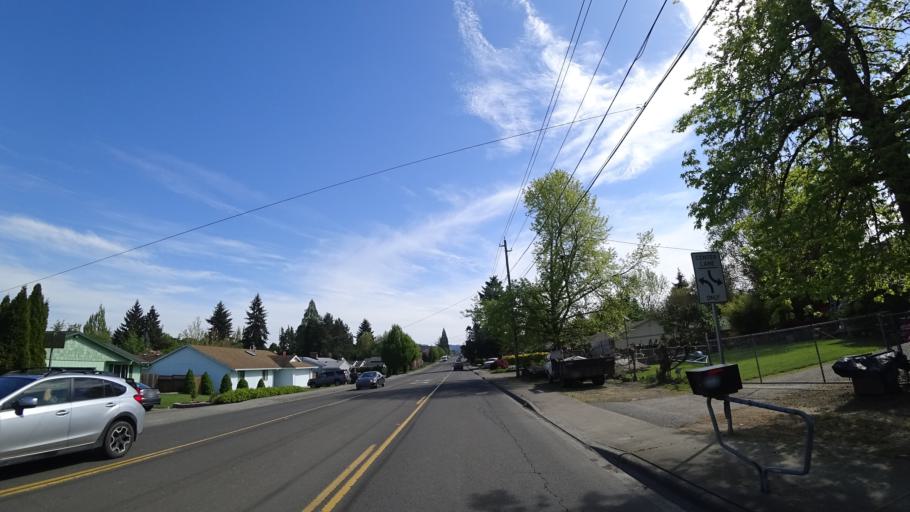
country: US
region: Oregon
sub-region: Washington County
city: Aloha
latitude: 45.4998
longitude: -122.8810
